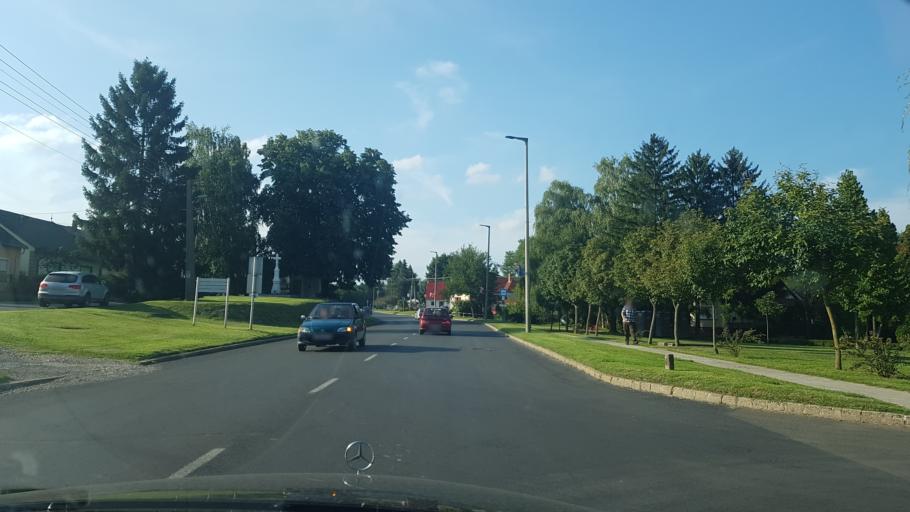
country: HU
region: Somogy
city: Nagyatad
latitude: 46.2378
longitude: 17.3567
